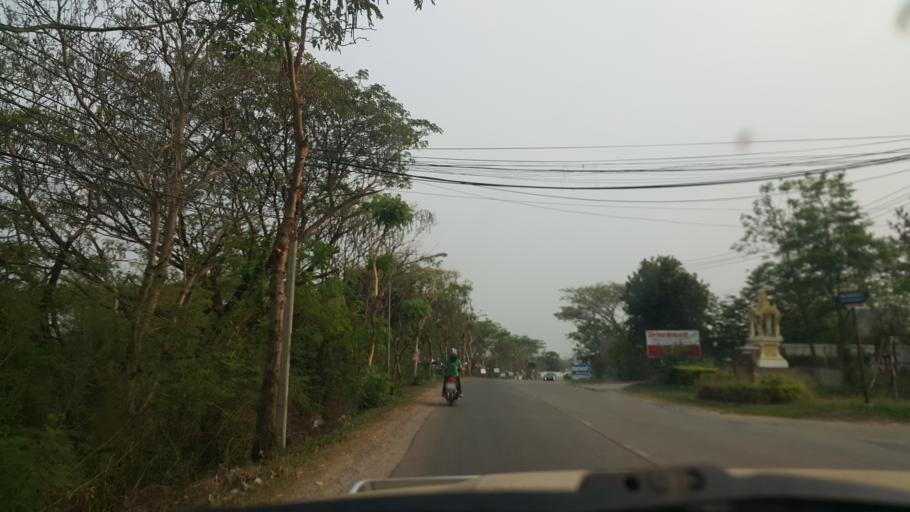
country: TH
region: Changwat Udon Thani
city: Udon Thani
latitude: 17.3924
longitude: 102.7713
